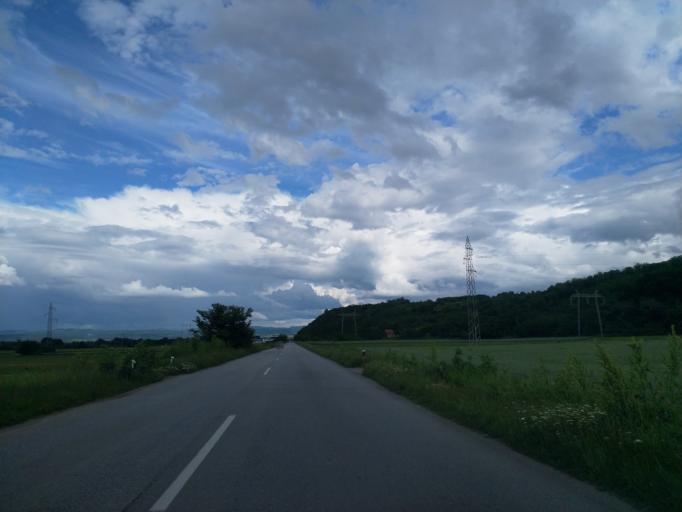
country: RS
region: Central Serbia
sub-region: Pomoravski Okrug
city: Jagodina
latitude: 43.9556
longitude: 21.3035
